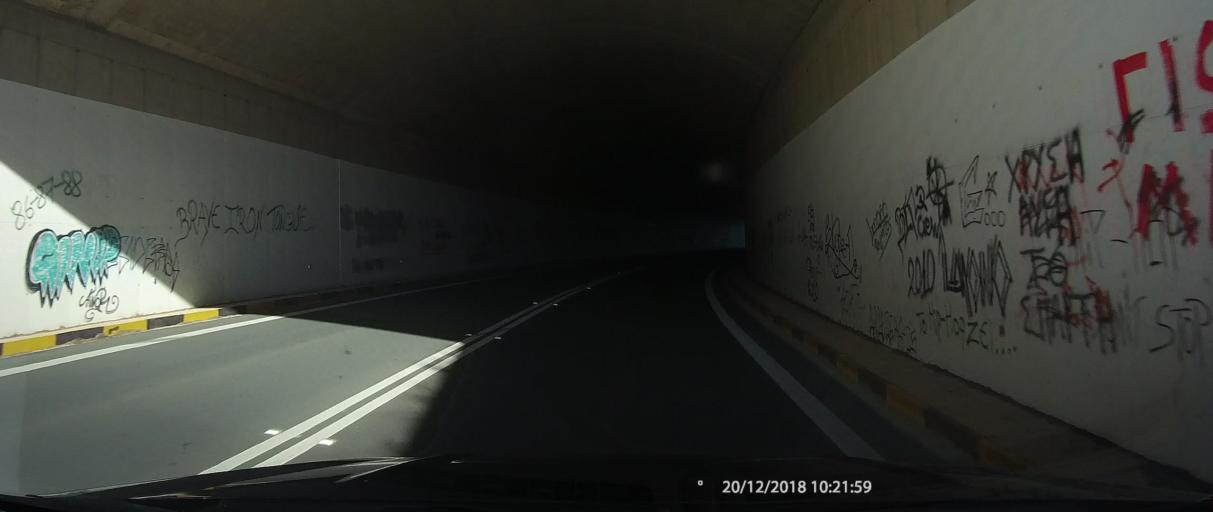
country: GR
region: Peloponnese
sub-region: Nomos Lakonias
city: Magoula
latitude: 37.1683
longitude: 22.4254
